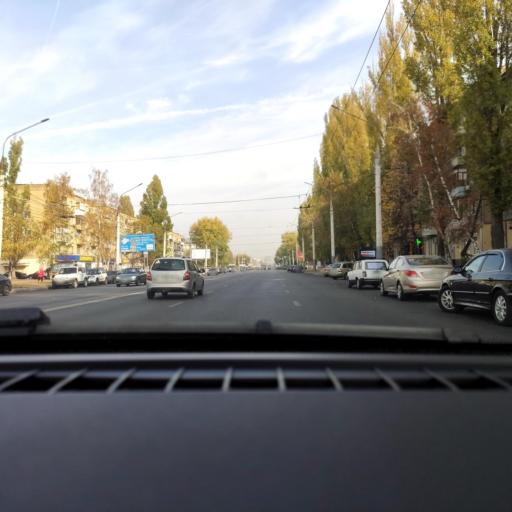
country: RU
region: Voronezj
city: Voronezh
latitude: 51.6533
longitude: 39.2428
